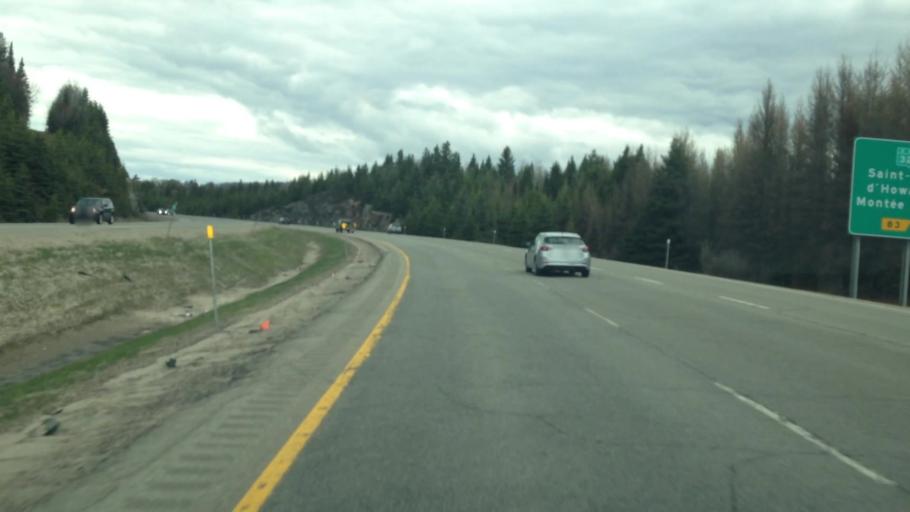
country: CA
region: Quebec
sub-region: Laurentides
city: Val-David
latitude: 46.0197
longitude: -74.2346
